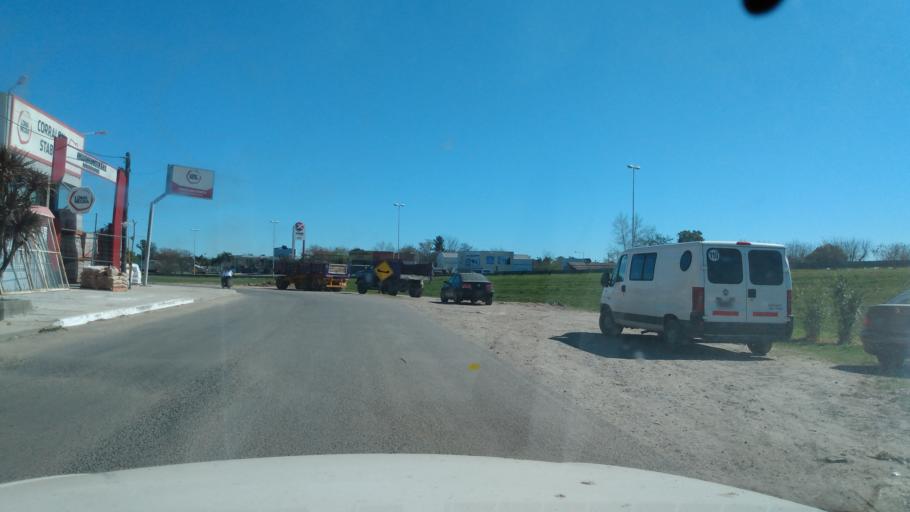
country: AR
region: Buenos Aires
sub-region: Partido de Lujan
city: Lujan
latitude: -34.5617
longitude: -59.0898
